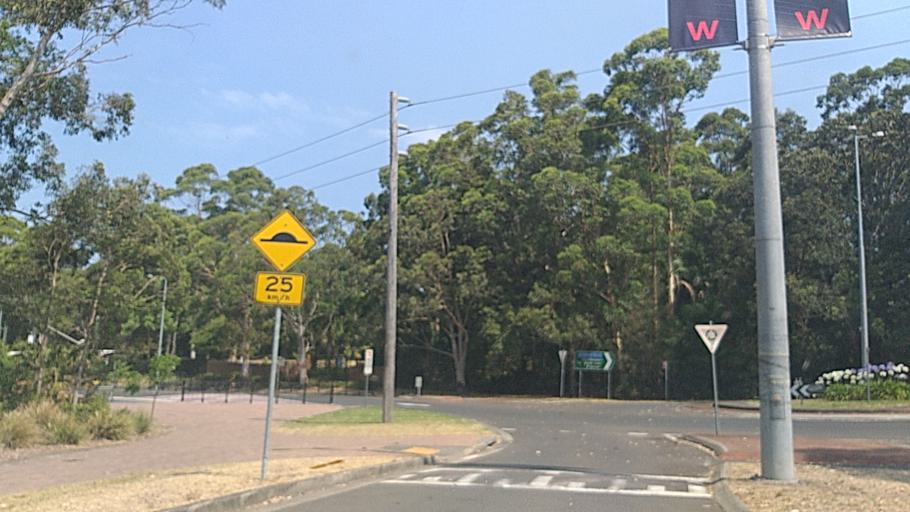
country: AU
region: New South Wales
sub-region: Wollongong
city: Mount Ousley
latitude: -34.4075
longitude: 150.8770
